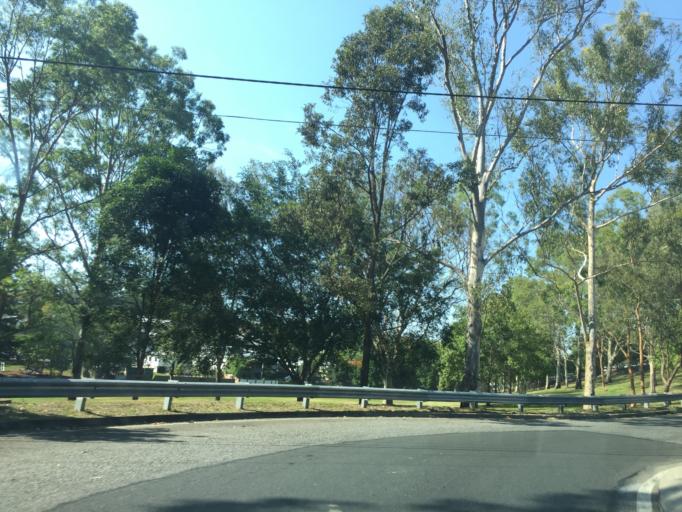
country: AU
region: Queensland
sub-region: Brisbane
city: Milton
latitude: -27.4650
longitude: 152.9888
